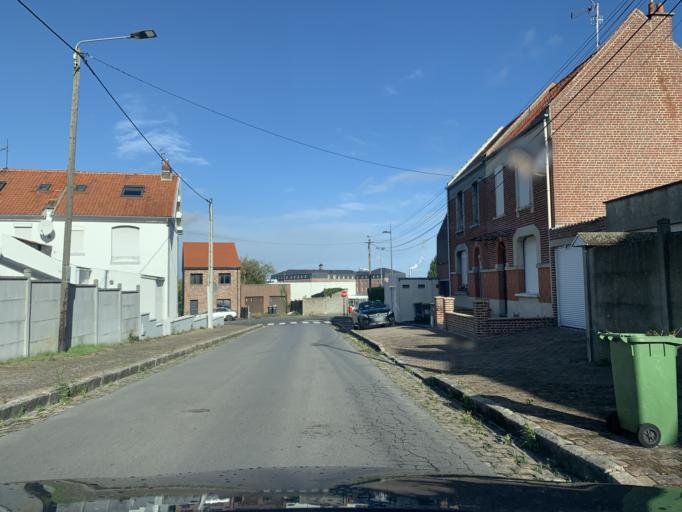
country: FR
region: Nord-Pas-de-Calais
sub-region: Departement du Nord
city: Escaudoeuvres
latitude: 50.1824
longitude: 3.2536
